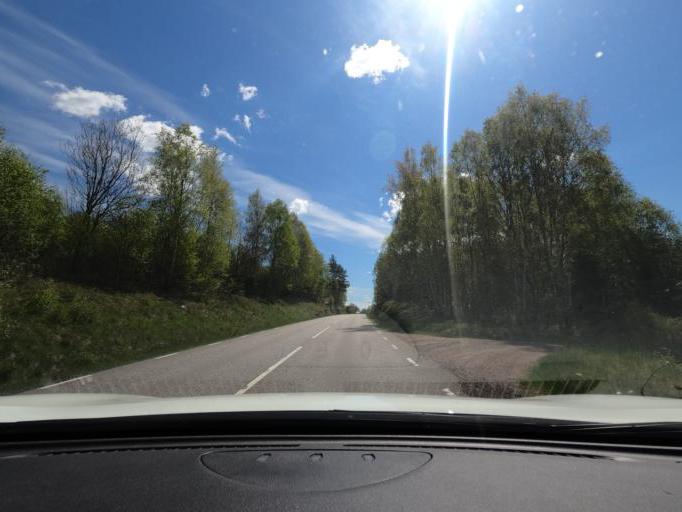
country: SE
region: Halland
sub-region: Kungsbacka Kommun
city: Fjaeras kyrkby
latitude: 57.4023
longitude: 12.2292
